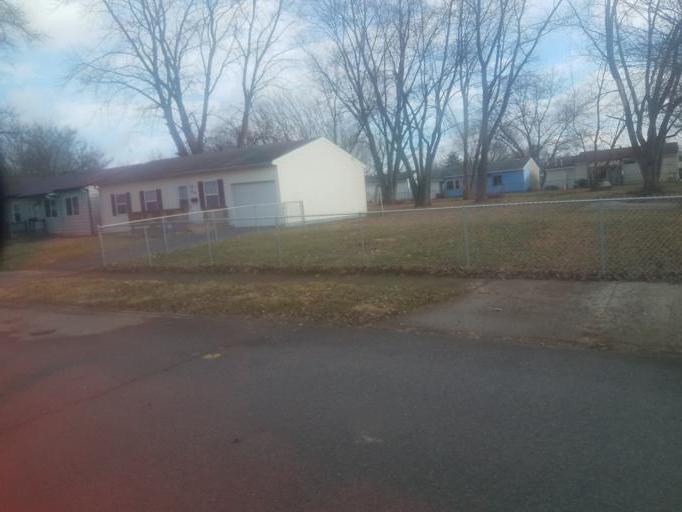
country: US
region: Ohio
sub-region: Marion County
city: Marion
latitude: 40.5803
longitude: -83.1529
